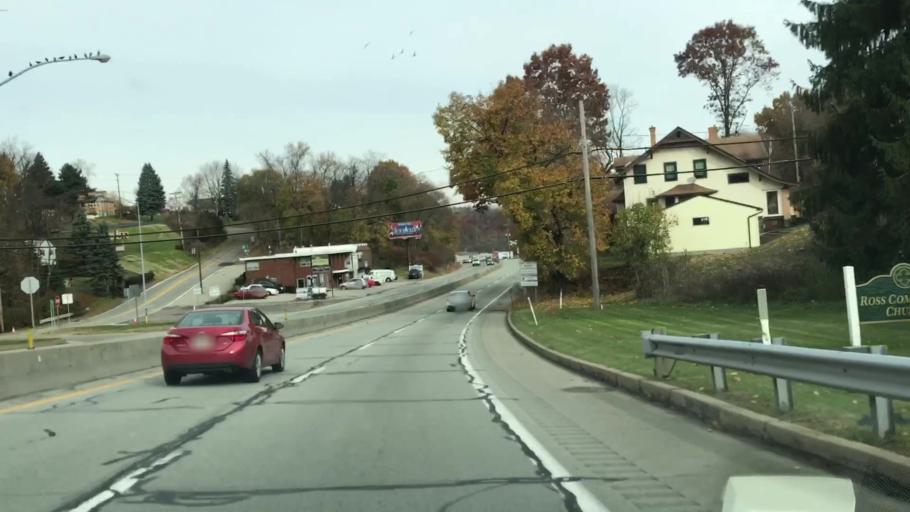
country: US
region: Pennsylvania
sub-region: Allegheny County
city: West View
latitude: 40.4996
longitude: -80.0127
